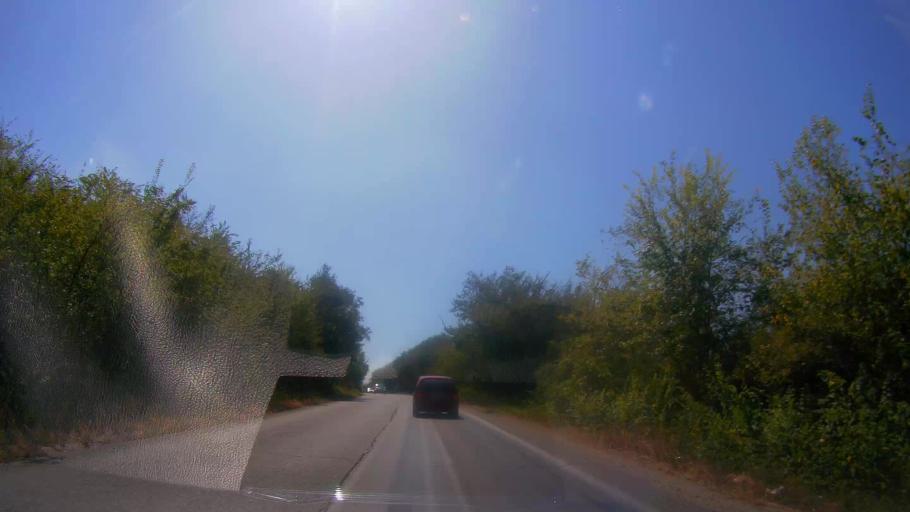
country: BG
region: Veliko Turnovo
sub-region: Obshtina Gorna Oryakhovitsa
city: Purvomaytsi
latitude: 43.2568
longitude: 25.6423
